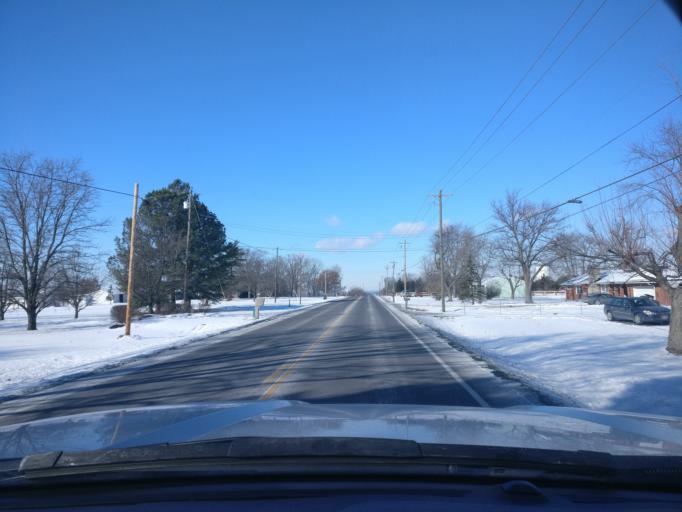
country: US
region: Ohio
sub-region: Warren County
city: Hunter
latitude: 39.5043
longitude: -84.2624
